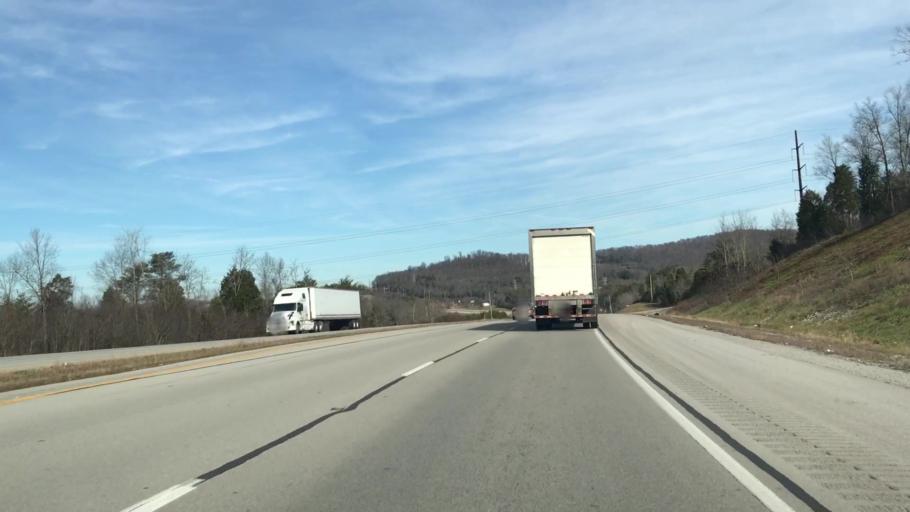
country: US
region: Kentucky
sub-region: Pulaski County
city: Somerset
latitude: 37.0168
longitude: -84.5990
